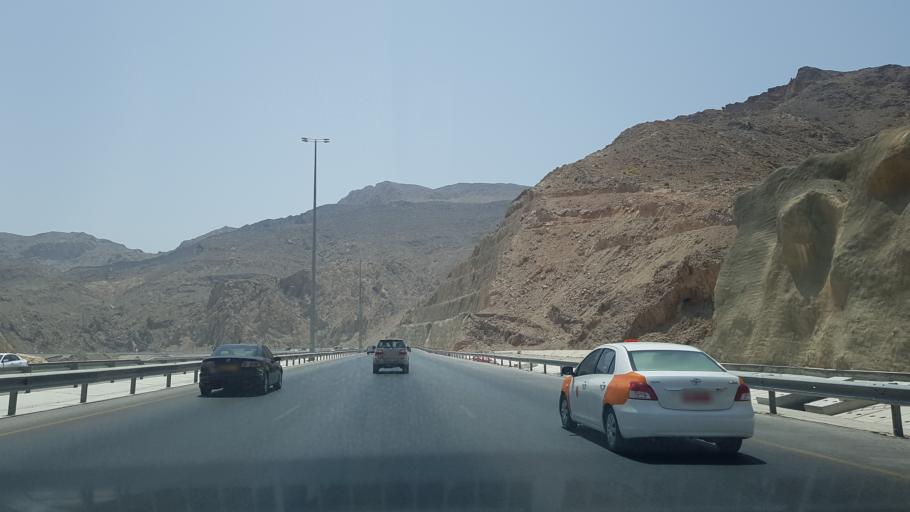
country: OM
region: Muhafazat Masqat
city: Muscat
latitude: 23.5708
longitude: 58.5241
